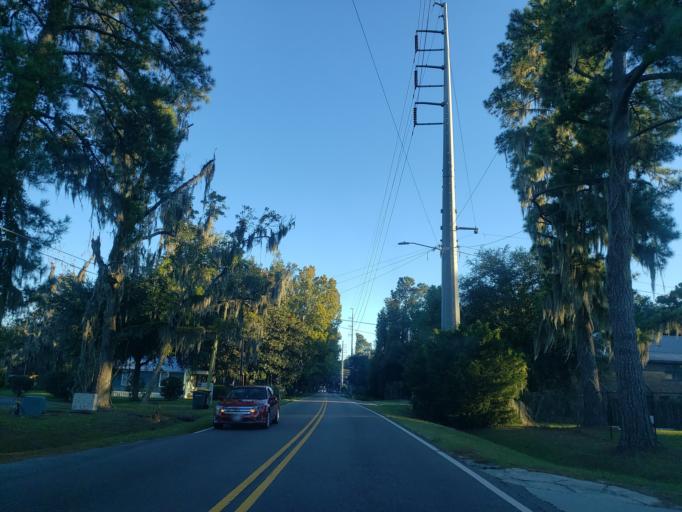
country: US
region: Georgia
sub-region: Chatham County
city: Isle of Hope
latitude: 31.9930
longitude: -81.0779
